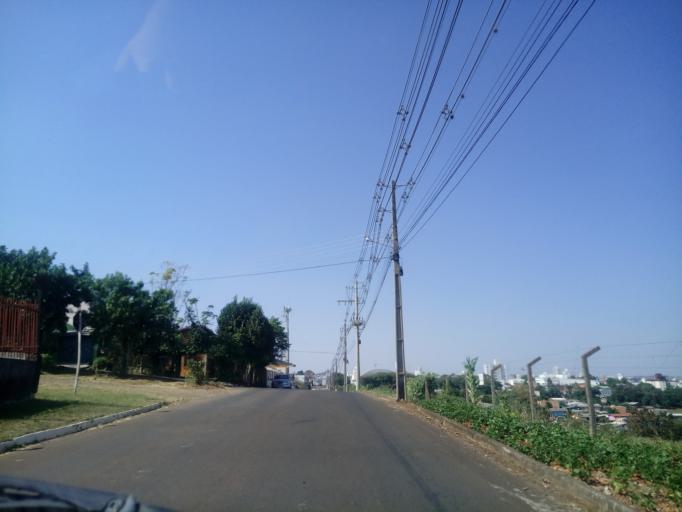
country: BR
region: Santa Catarina
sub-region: Chapeco
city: Chapeco
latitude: -27.0838
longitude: -52.6337
